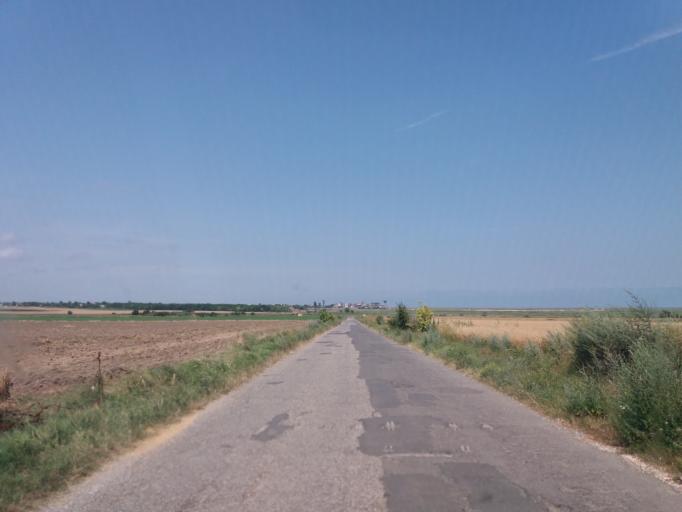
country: RO
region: Constanta
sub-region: Comuna Sacele
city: Sacele
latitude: 44.4349
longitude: 28.7213
